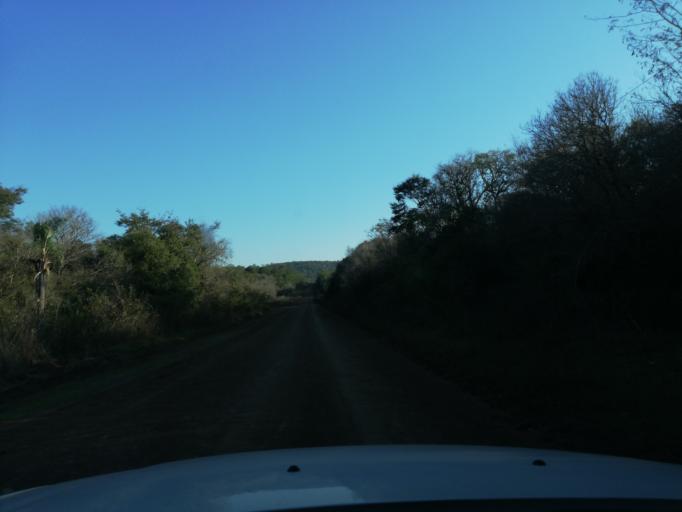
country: AR
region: Misiones
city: Cerro Cora
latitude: -27.5993
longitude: -55.6983
